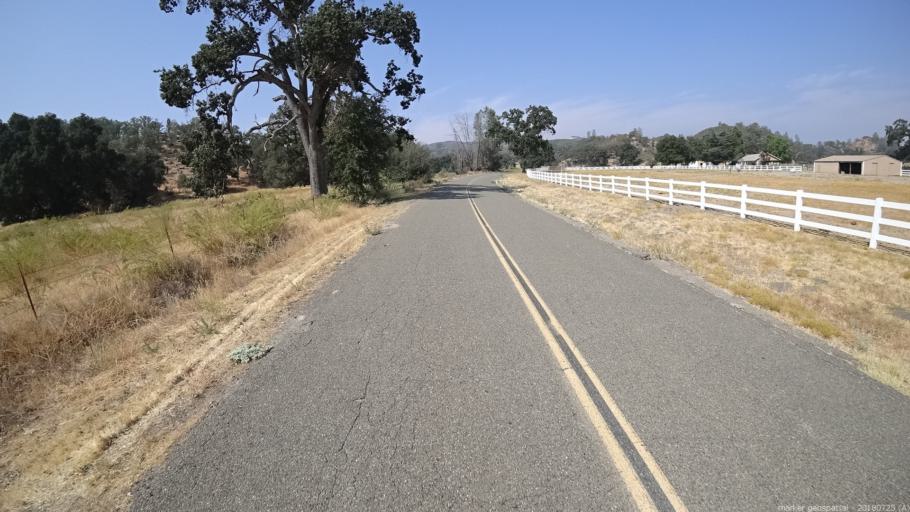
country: US
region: California
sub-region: San Luis Obispo County
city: San Miguel
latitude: 35.9253
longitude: -120.5053
